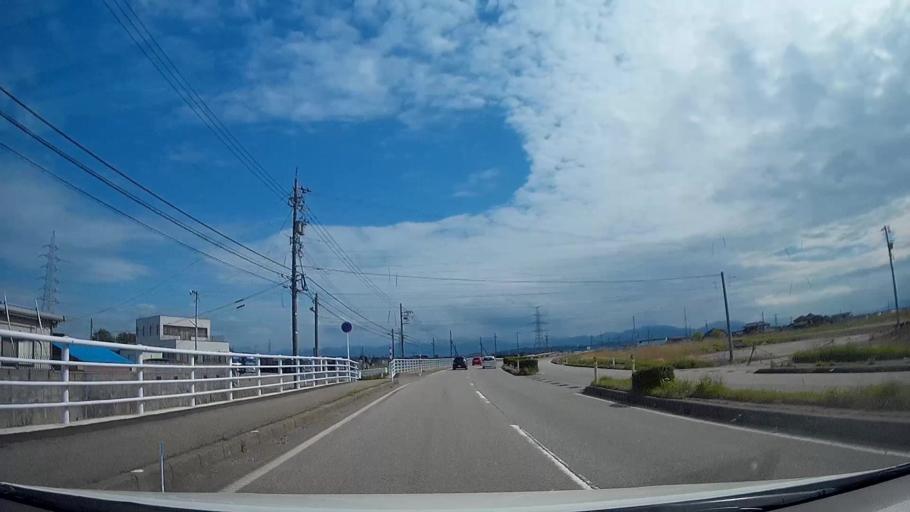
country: JP
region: Toyama
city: Kuragaki-kosugi
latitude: 36.7399
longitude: 137.1300
